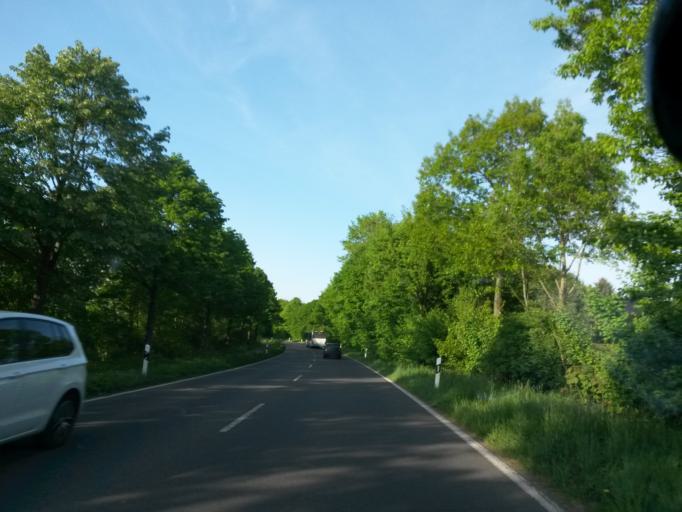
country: DE
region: North Rhine-Westphalia
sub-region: Regierungsbezirk Koln
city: Overath
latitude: 50.8762
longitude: 7.3351
